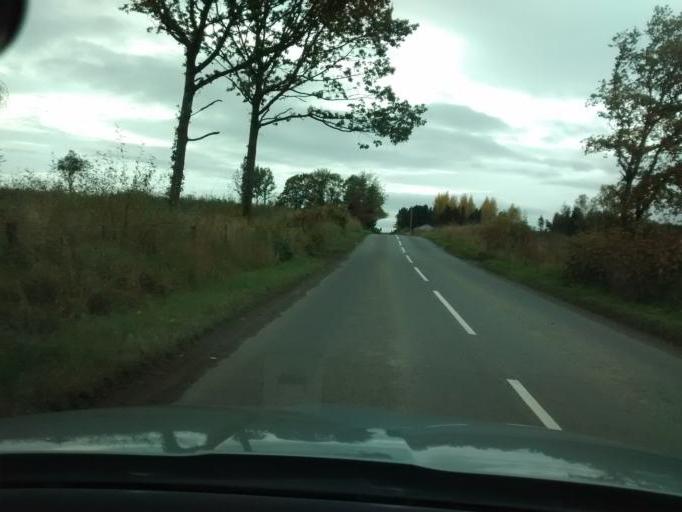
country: GB
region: Scotland
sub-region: Perth and Kinross
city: Stanley
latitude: 56.4963
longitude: -3.4366
